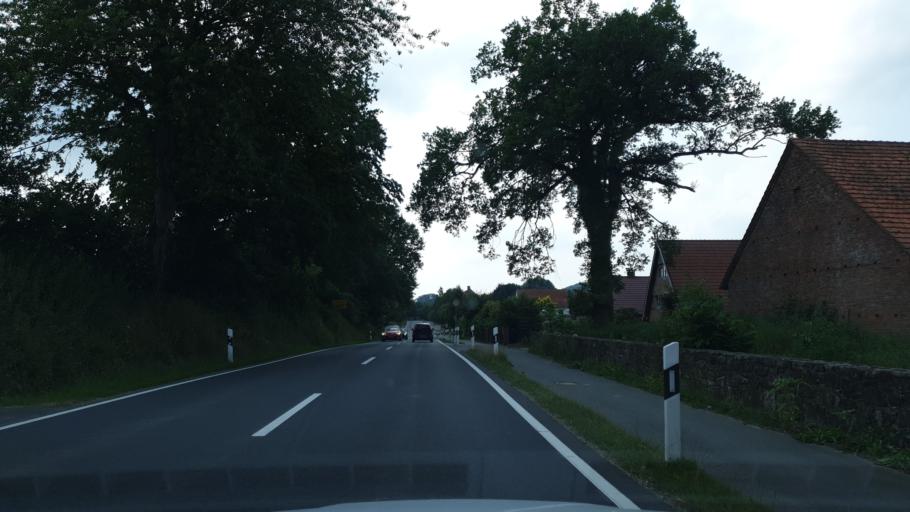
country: DE
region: North Rhine-Westphalia
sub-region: Regierungsbezirk Detmold
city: Bad Salzuflen
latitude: 52.1375
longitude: 8.7734
